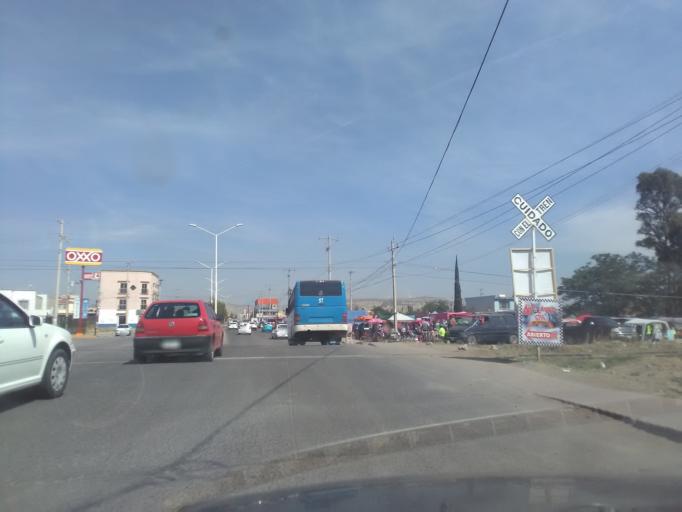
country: MX
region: Durango
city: Victoria de Durango
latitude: 24.0562
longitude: -104.6289
